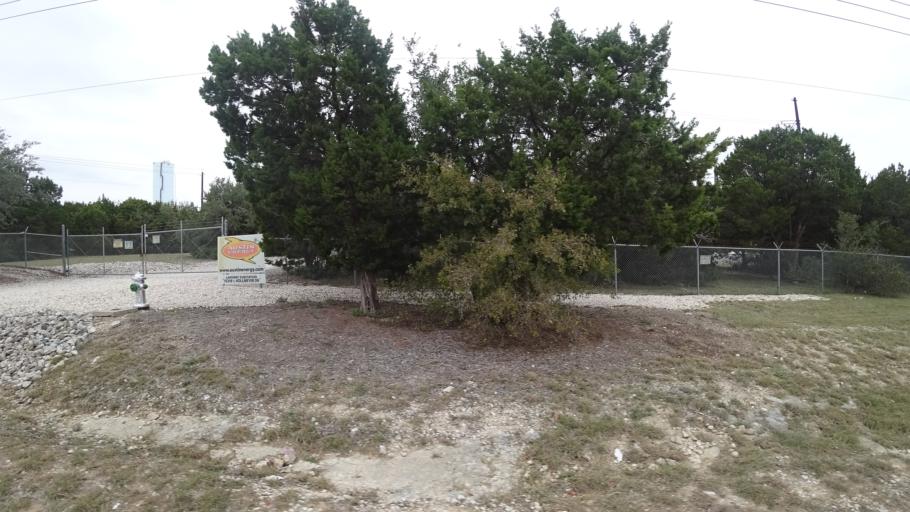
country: US
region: Texas
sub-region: Travis County
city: Lakeway
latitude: 30.3713
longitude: -97.9453
